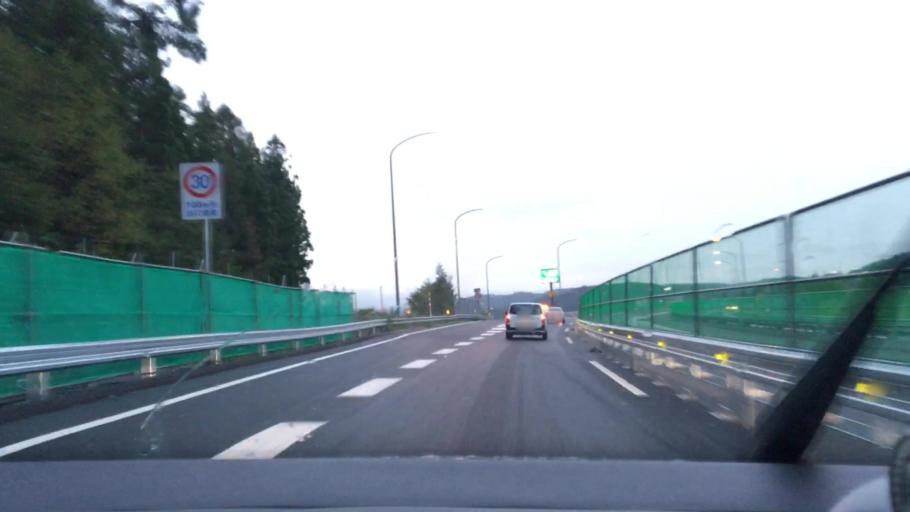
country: JP
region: Gifu
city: Gujo
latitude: 35.9343
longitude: 136.8790
